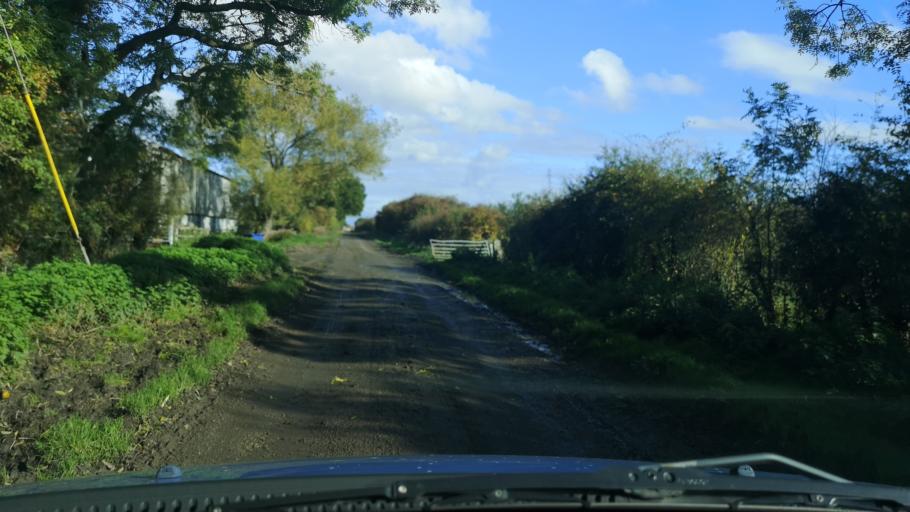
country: GB
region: England
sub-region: Doncaster
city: Moss
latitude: 53.6268
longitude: -1.1222
